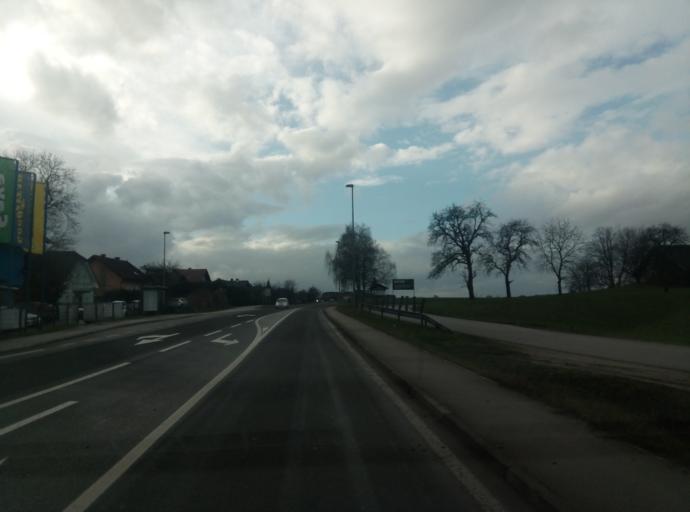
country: SI
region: Lukovica
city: Lukovica pri Domzalah
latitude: 46.1622
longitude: 14.6702
